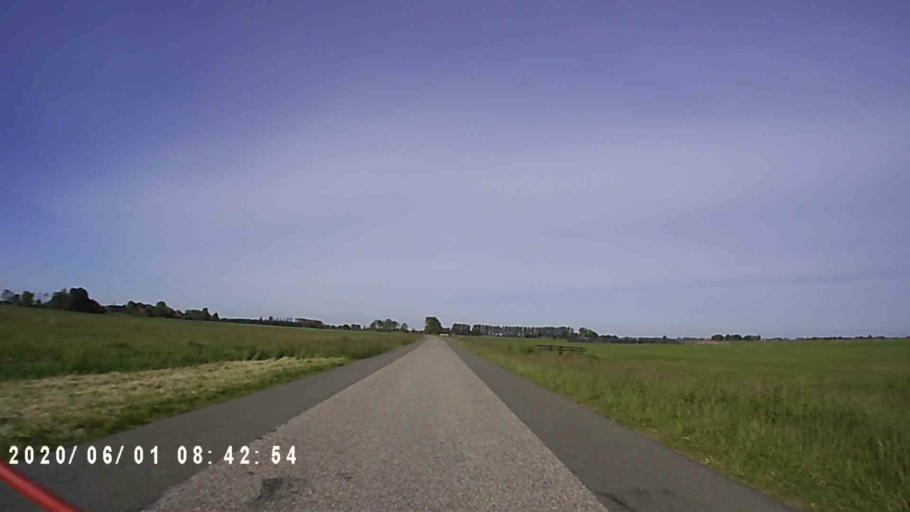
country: NL
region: Friesland
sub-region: Gemeente Ferwerderadiel
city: Burdaard
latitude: 53.2849
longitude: 5.8446
